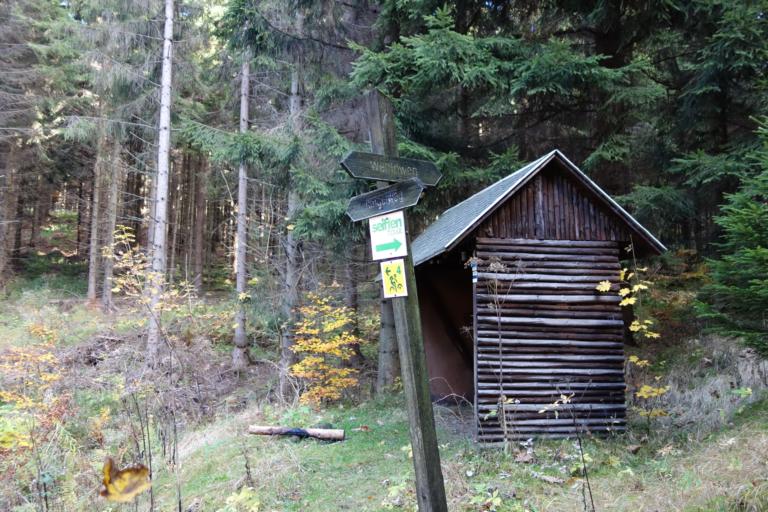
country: DE
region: Saxony
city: Seiffen
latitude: 50.6439
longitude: 13.4165
